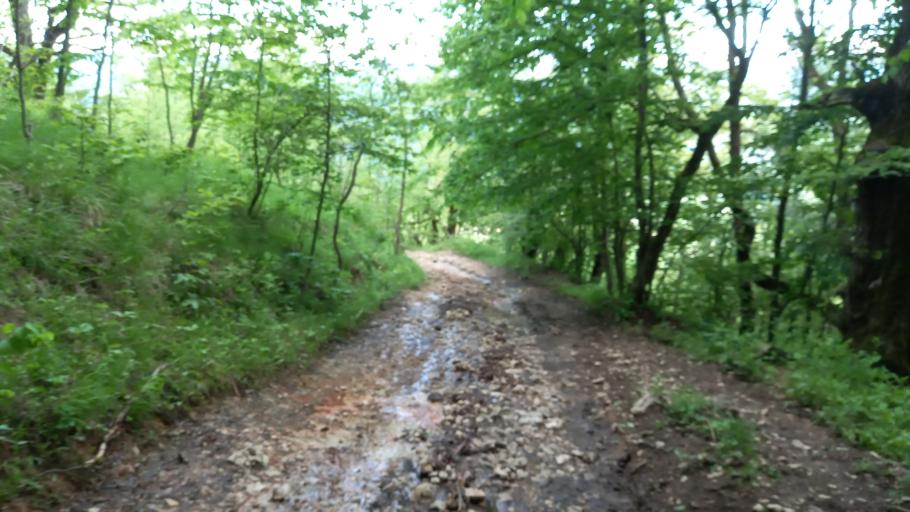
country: RU
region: Adygeya
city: Kamennomostskiy
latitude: 44.2219
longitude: 40.0019
